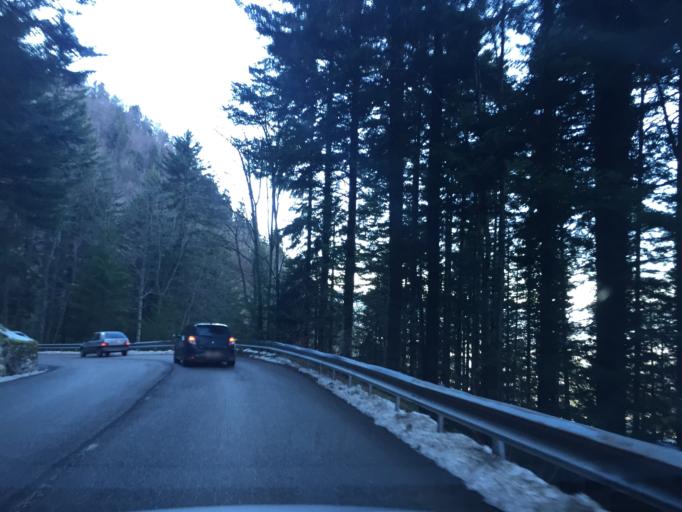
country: FR
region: Rhone-Alpes
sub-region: Departement de la Haute-Savoie
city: Cusy
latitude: 45.7016
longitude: 6.0043
